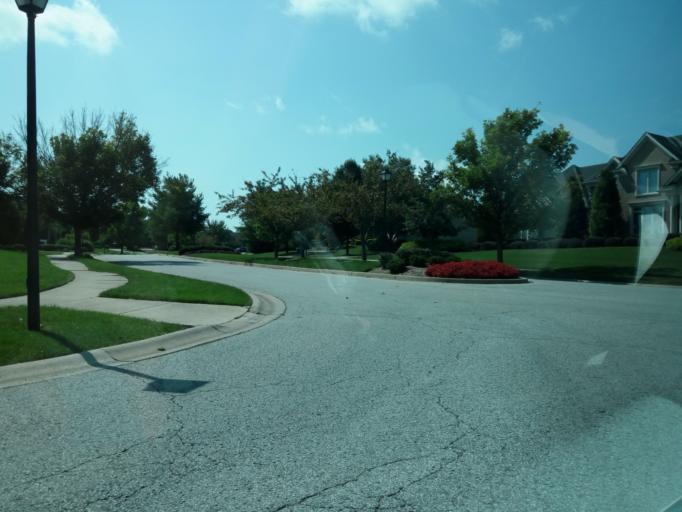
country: US
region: Kentucky
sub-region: Oldham County
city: Pewee Valley
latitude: 38.2725
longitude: -85.4805
